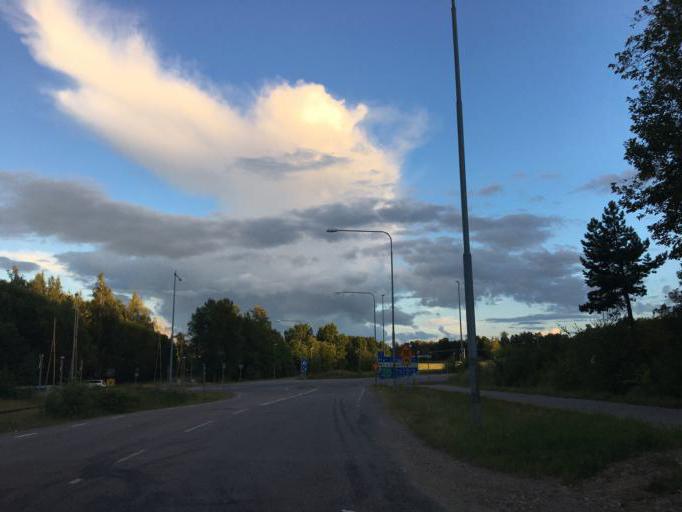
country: SE
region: Soedermanland
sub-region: Eskilstuna Kommun
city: Torshalla
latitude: 59.4182
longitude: 16.4614
